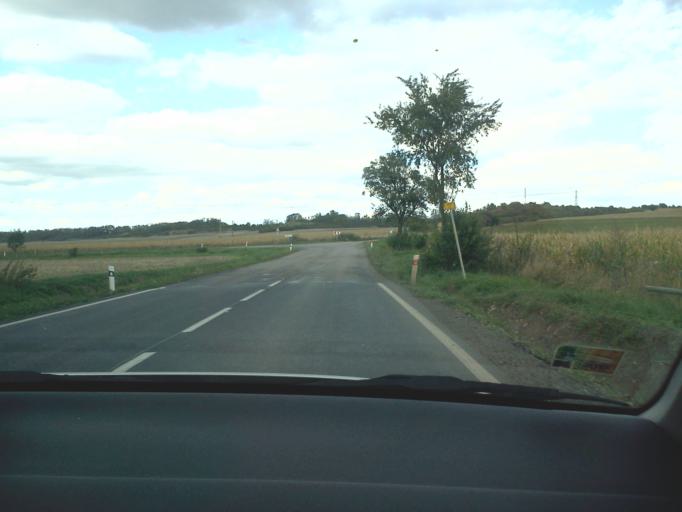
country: CZ
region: Central Bohemia
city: Cesky Brod
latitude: 50.1140
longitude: 14.8615
